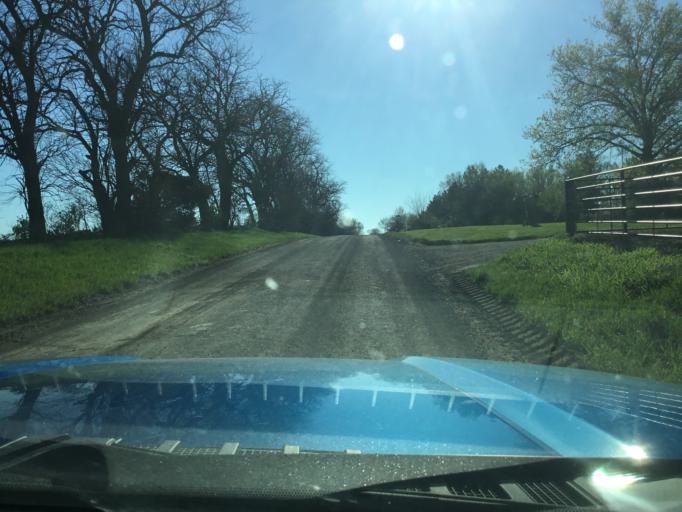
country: US
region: Kansas
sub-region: Douglas County
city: Lawrence
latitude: 38.9569
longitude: -95.3674
